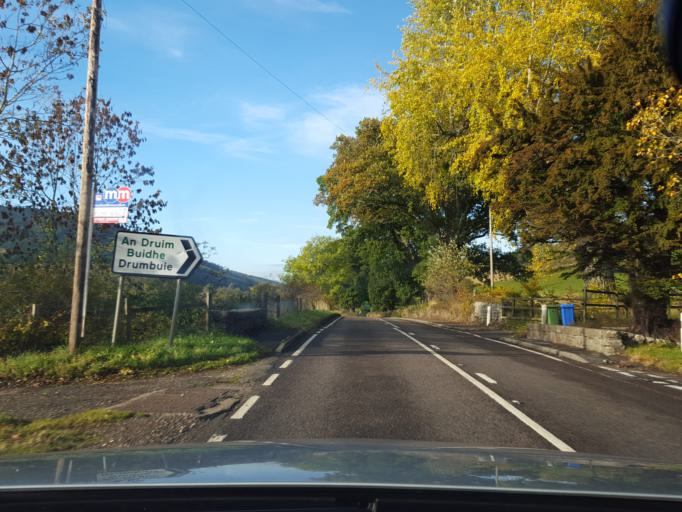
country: GB
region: Scotland
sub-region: Highland
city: Beauly
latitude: 57.3373
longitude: -4.4657
